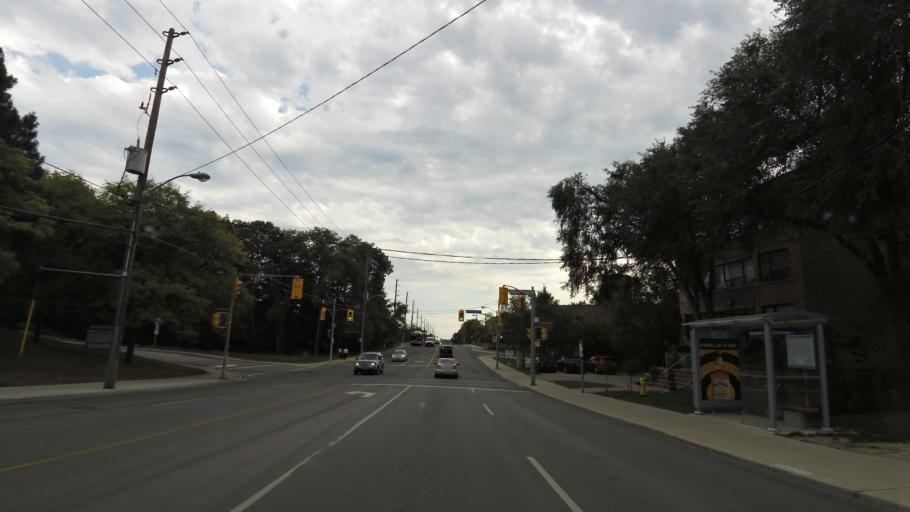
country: CA
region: Ontario
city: Toronto
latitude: 43.6969
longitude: -79.4754
